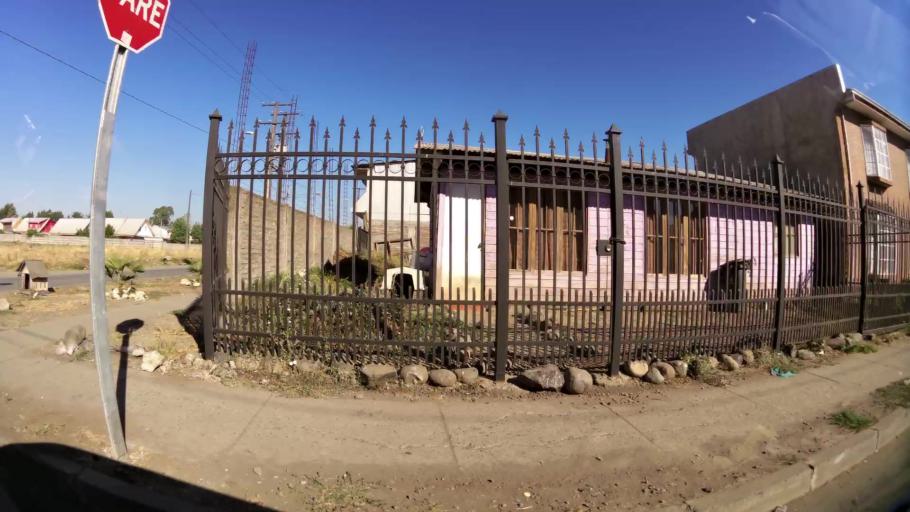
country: CL
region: Maule
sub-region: Provincia de Curico
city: Curico
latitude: -34.9892
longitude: -71.2557
